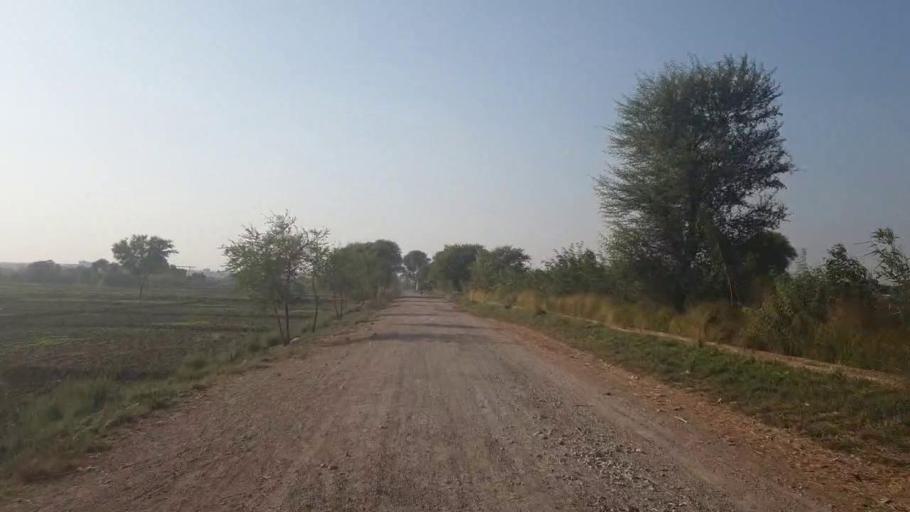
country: PK
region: Sindh
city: Jamshoro
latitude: 25.4008
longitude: 68.2924
